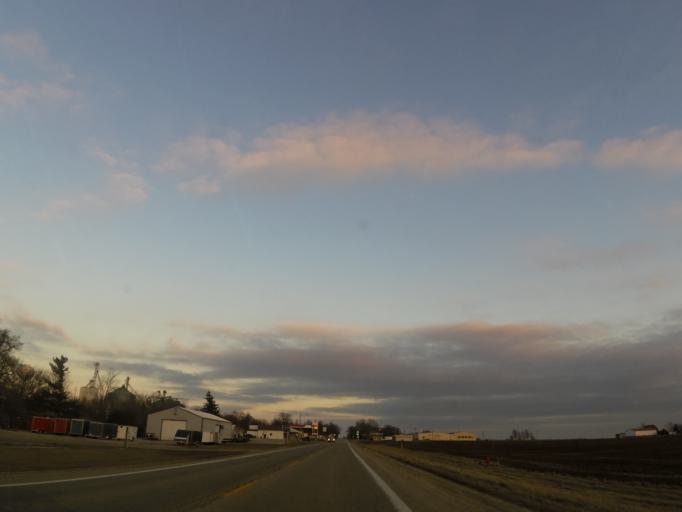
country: US
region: Illinois
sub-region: McLean County
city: Gridley
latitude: 40.7396
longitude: -88.8869
